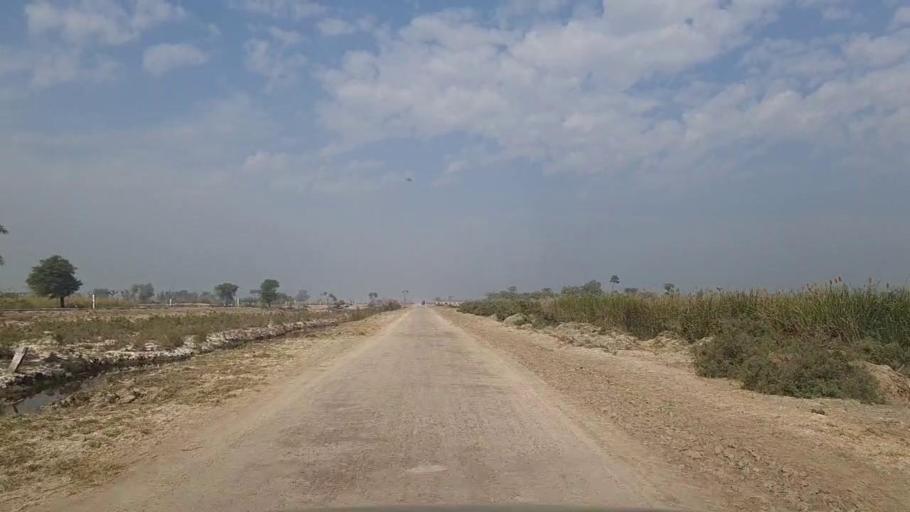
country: PK
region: Sindh
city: Daur
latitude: 26.3808
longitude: 68.3545
